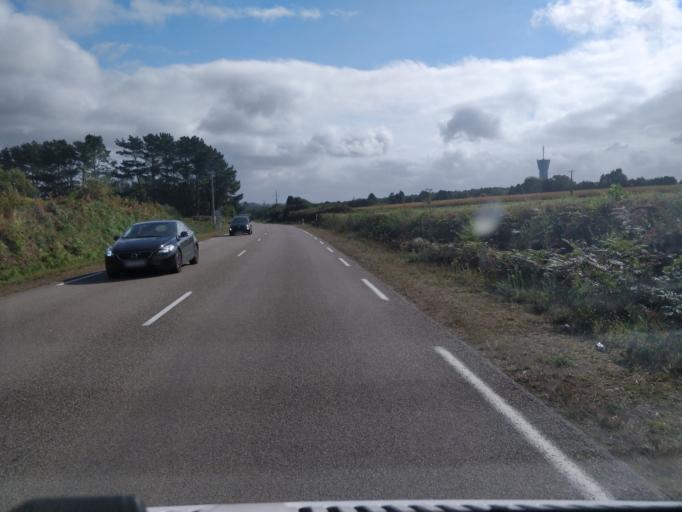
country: FR
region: Brittany
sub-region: Departement du Finistere
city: Plozevet
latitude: 47.9950
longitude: -4.3854
